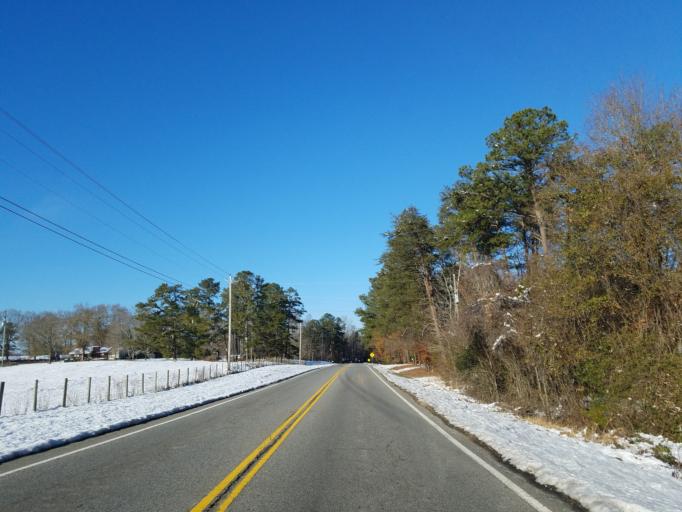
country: US
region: Georgia
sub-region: Dawson County
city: Dawsonville
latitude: 34.3383
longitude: -84.1191
